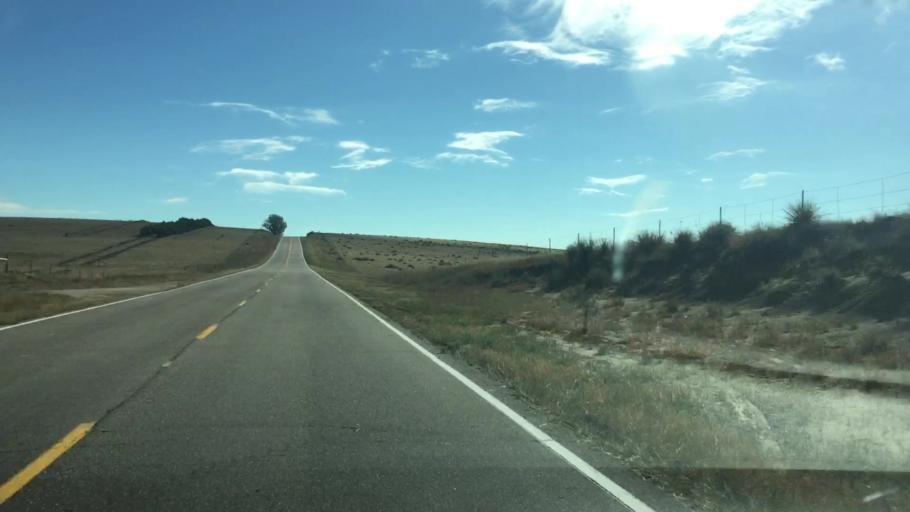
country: US
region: Colorado
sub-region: Elbert County
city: Kiowa
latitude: 39.2736
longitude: -104.2159
